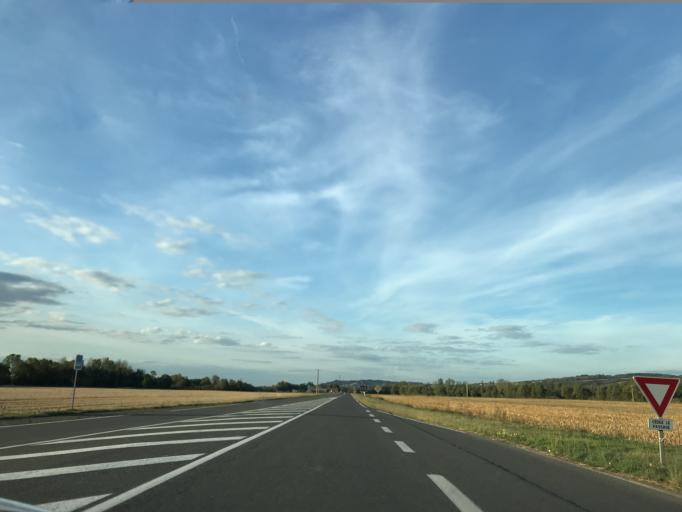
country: FR
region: Auvergne
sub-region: Departement de l'Allier
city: Saint-Yorre
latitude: 46.0286
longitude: 3.4779
